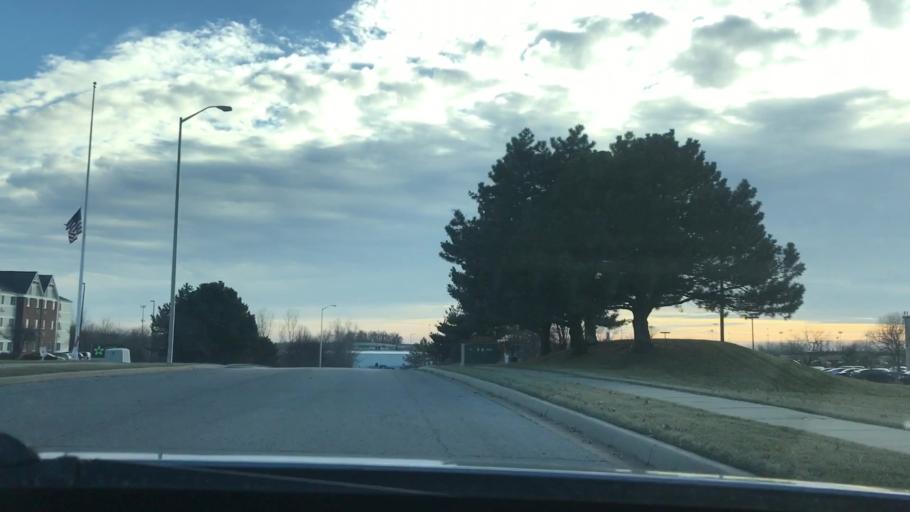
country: US
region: Missouri
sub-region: Platte County
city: Weatherby Lake
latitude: 39.2696
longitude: -94.6695
